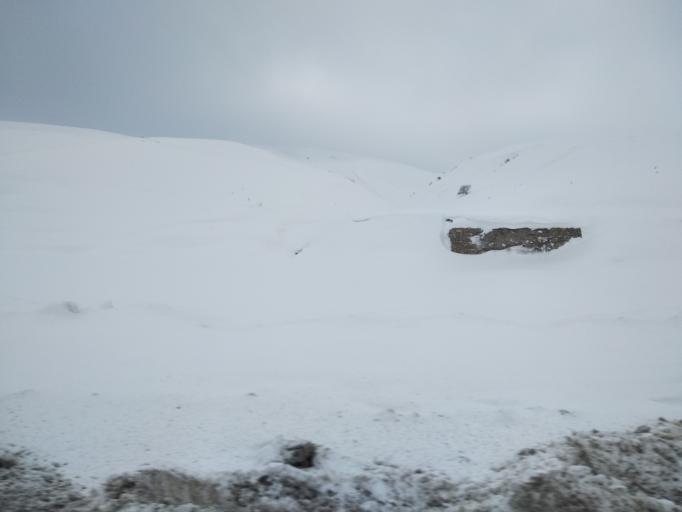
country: TR
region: Erzincan
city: Catalarmut
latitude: 39.8894
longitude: 39.3550
